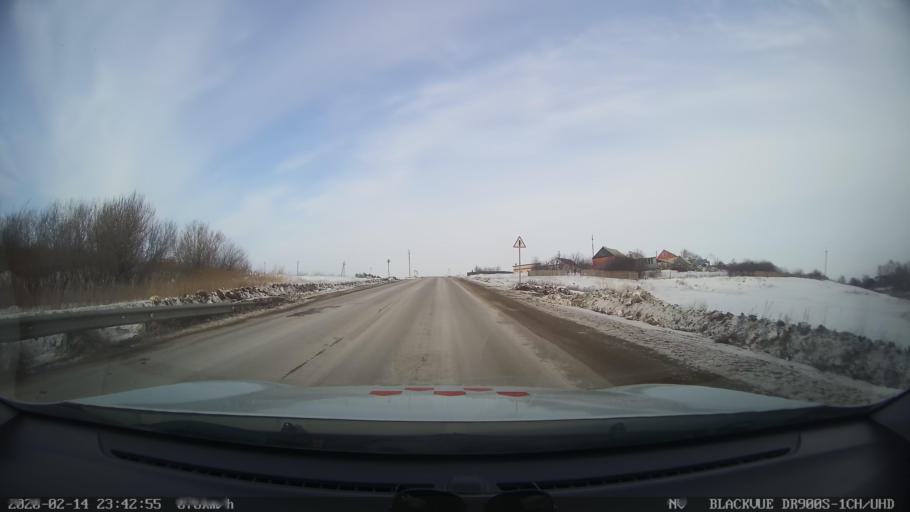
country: RU
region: Tatarstan
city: Kuybyshevskiy Zaton
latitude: 55.1962
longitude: 49.2478
